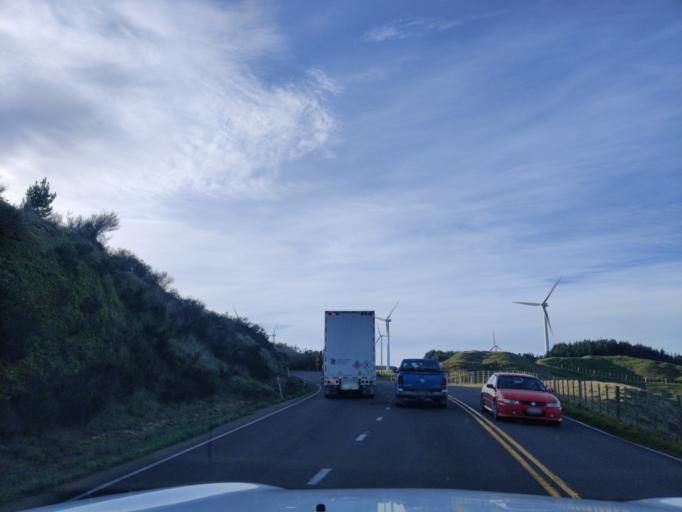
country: NZ
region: Manawatu-Wanganui
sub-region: Palmerston North City
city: Palmerston North
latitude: -40.2902
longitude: 175.8000
